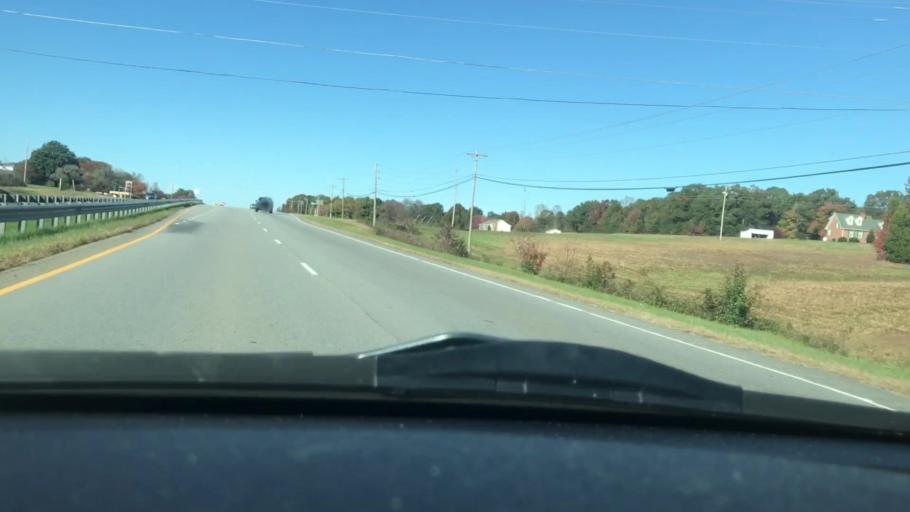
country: US
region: North Carolina
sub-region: Rockingham County
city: Madison
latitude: 36.3433
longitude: -79.9439
